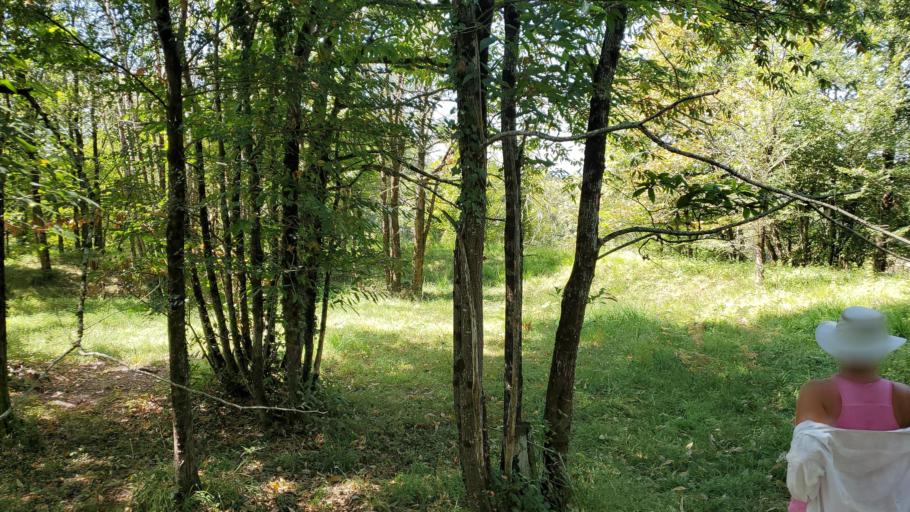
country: FR
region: Aquitaine
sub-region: Departement des Pyrenees-Atlantiques
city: Navarrenx
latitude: 43.3189
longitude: -0.7275
